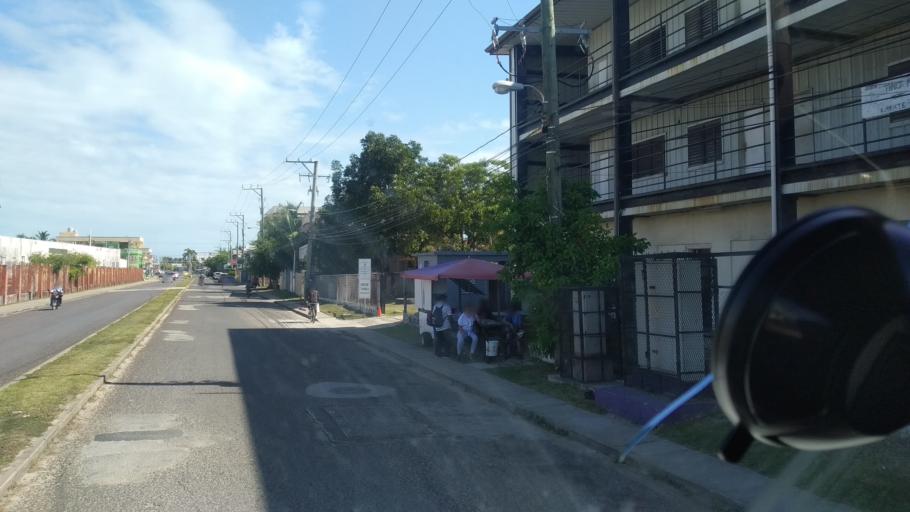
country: BZ
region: Belize
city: Belize City
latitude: 17.5057
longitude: -88.1948
